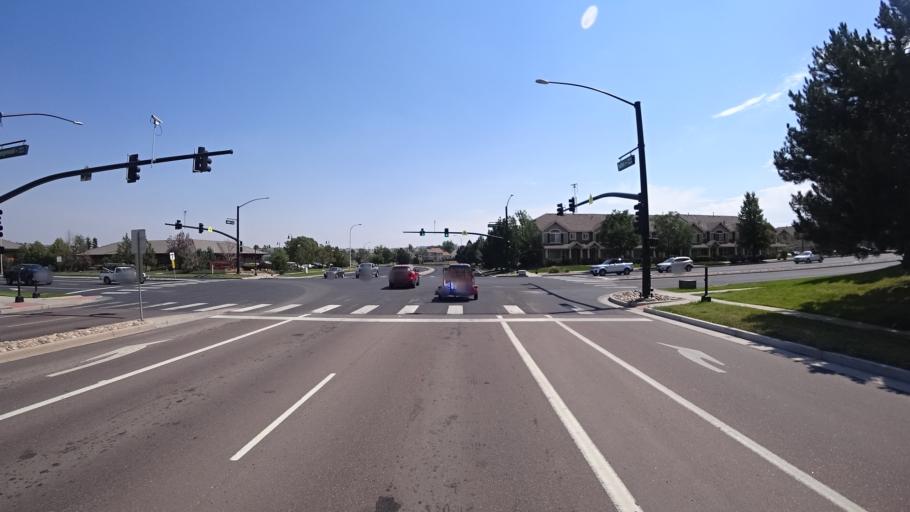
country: US
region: Colorado
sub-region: El Paso County
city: Cimarron Hills
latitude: 38.9268
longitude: -104.7523
